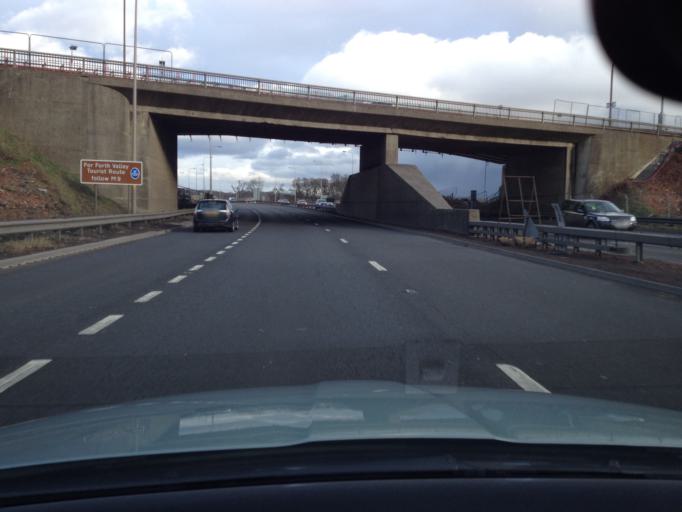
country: GB
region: Scotland
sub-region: Edinburgh
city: Queensferry
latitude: 55.9798
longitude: -3.3975
